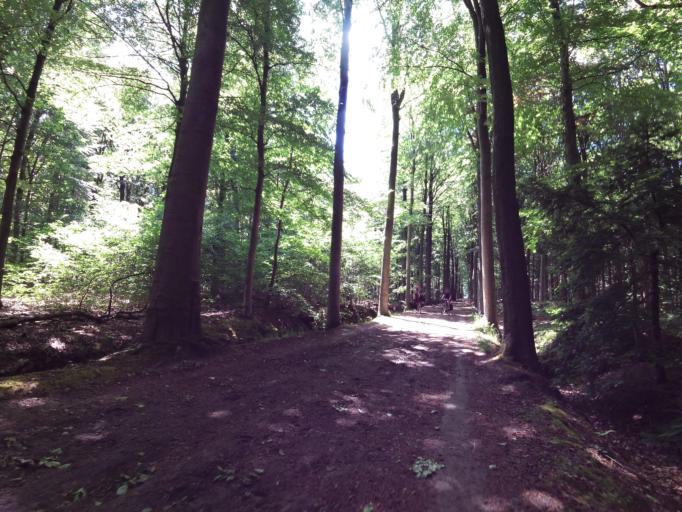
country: BE
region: Flanders
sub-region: Provincie West-Vlaanderen
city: Zedelgem
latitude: 51.1522
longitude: 3.1165
